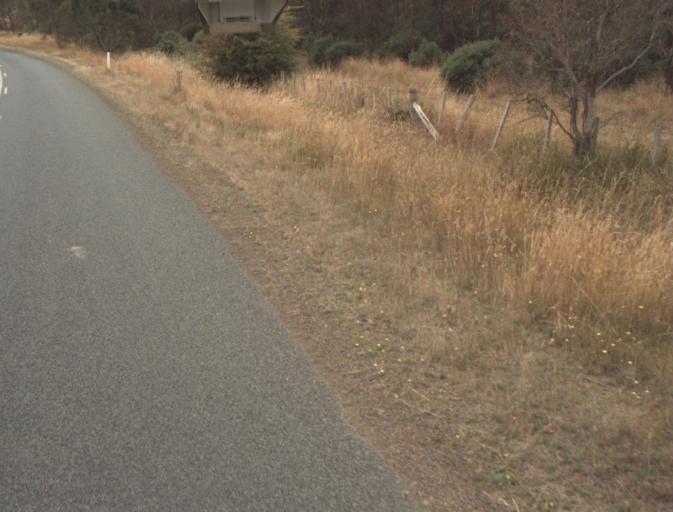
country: AU
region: Tasmania
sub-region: Northern Midlands
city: Evandale
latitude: -41.4848
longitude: 147.5035
